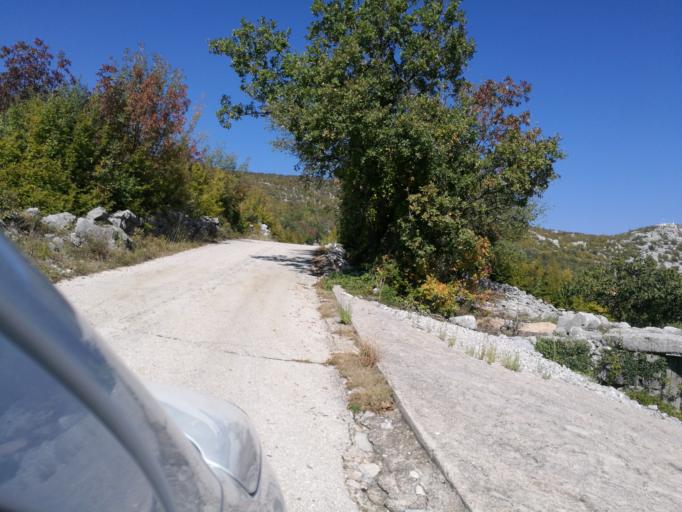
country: HR
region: Splitsko-Dalmatinska
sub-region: Grad Omis
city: Omis
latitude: 43.5152
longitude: 16.7279
